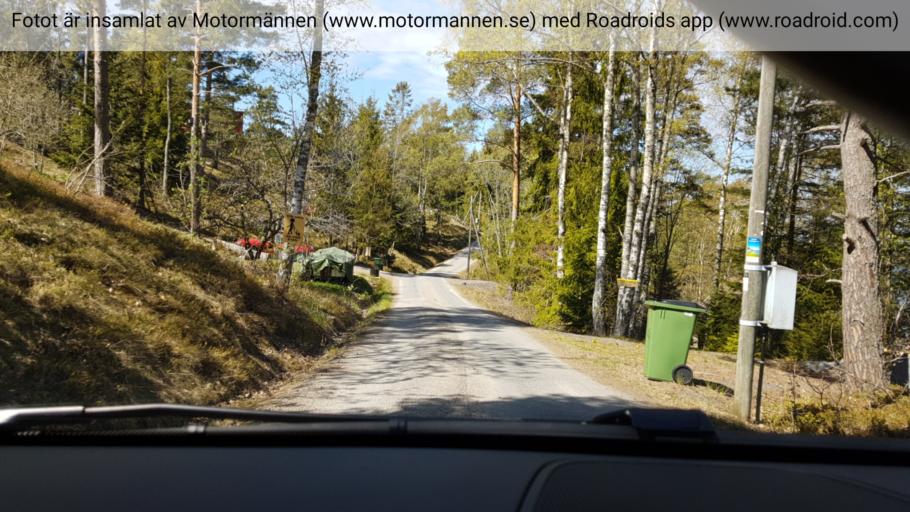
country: SE
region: Stockholm
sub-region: Haninge Kommun
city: Jordbro
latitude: 59.0178
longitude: 18.1138
